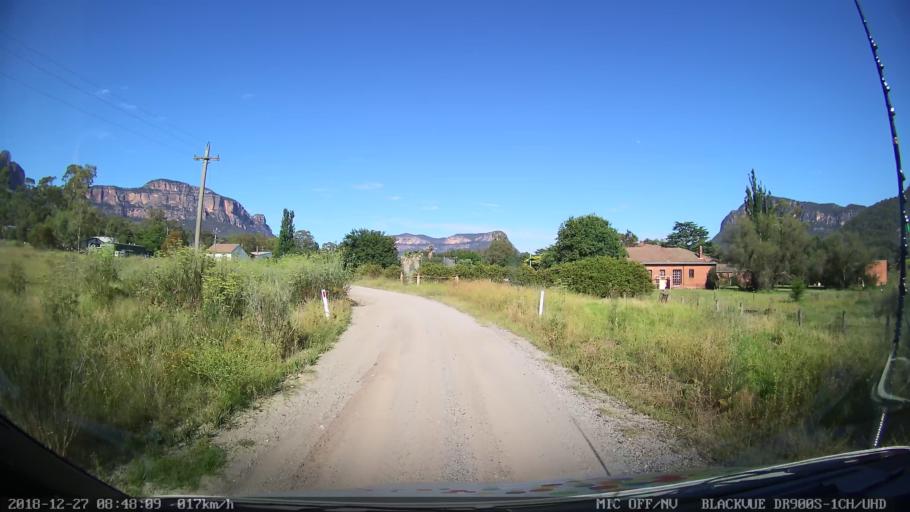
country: AU
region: New South Wales
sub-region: Lithgow
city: Portland
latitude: -33.1229
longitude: 150.2832
